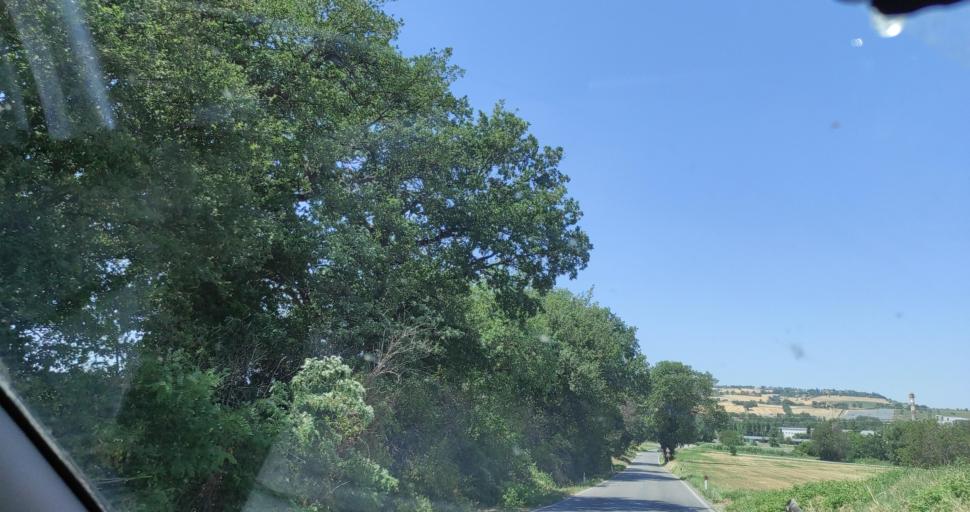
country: IT
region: The Marches
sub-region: Provincia di Macerata
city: Casette Verdini
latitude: 43.2336
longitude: 13.3918
